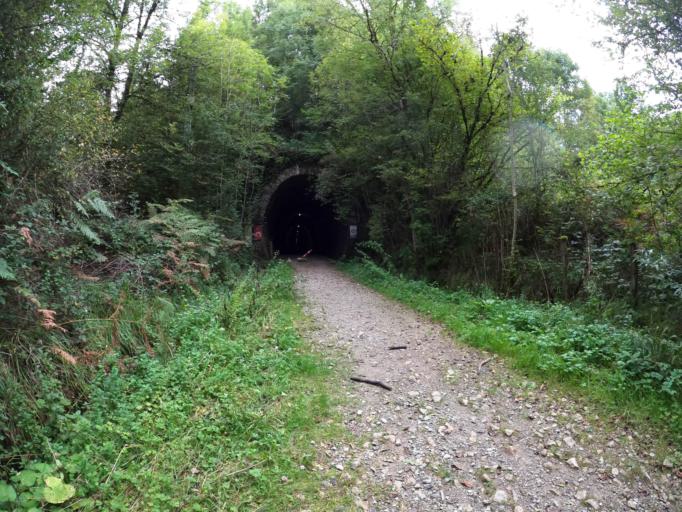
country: ES
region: Navarre
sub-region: Provincia de Navarra
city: Lekunberri
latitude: 43.0314
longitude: -1.9050
